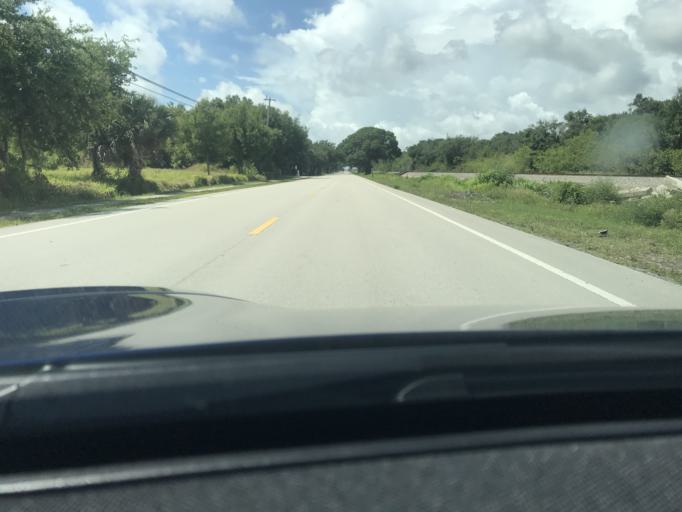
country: US
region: Florida
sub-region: Indian River County
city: Winter Beach
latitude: 27.7067
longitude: -80.4189
